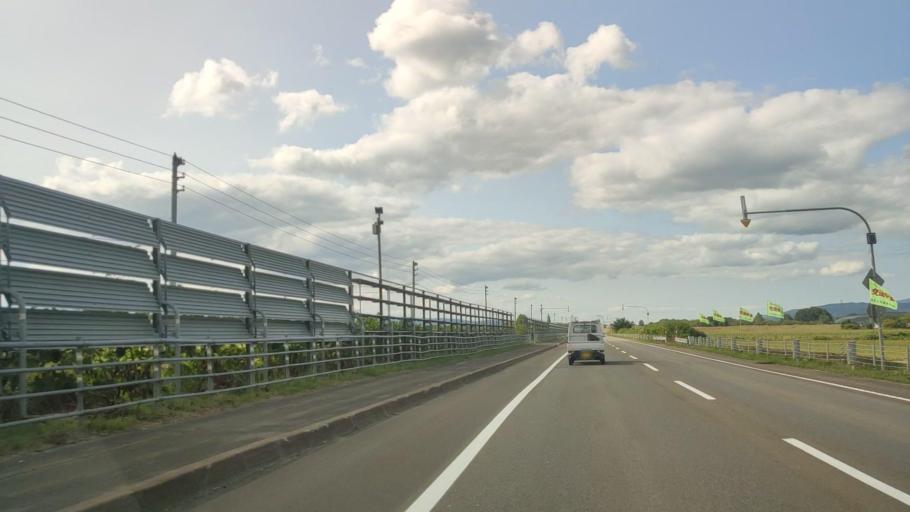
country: JP
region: Hokkaido
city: Nayoro
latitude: 44.4476
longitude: 142.3627
